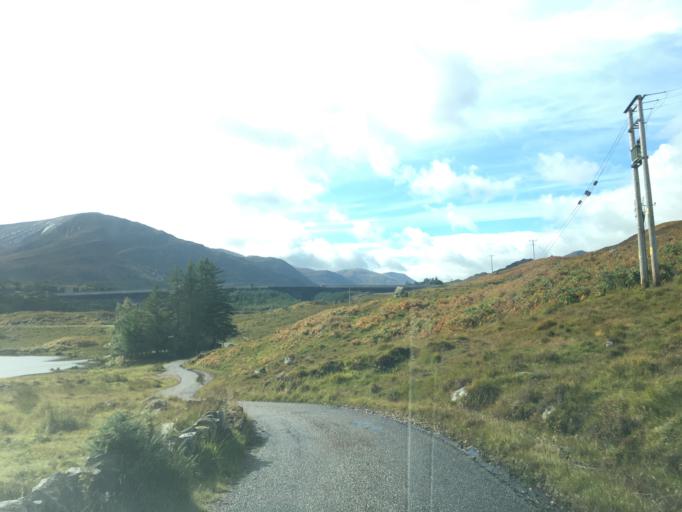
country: GB
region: Scotland
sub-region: Highland
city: Spean Bridge
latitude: 57.3427
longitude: -4.9420
